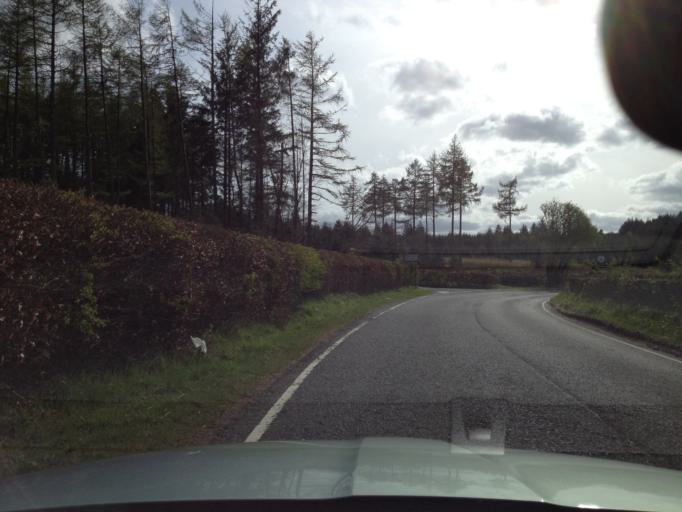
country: GB
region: Scotland
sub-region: West Lothian
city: Linlithgow
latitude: 55.9537
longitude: -3.6049
